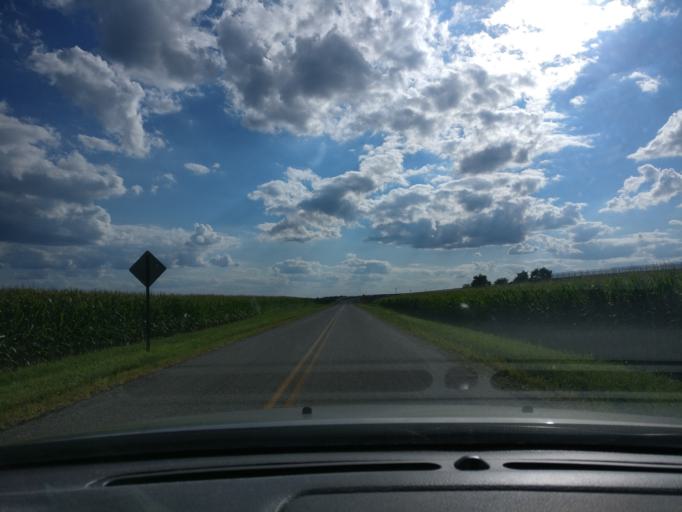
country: US
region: Ohio
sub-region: Greene County
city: Jamestown
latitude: 39.5476
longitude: -83.7447
